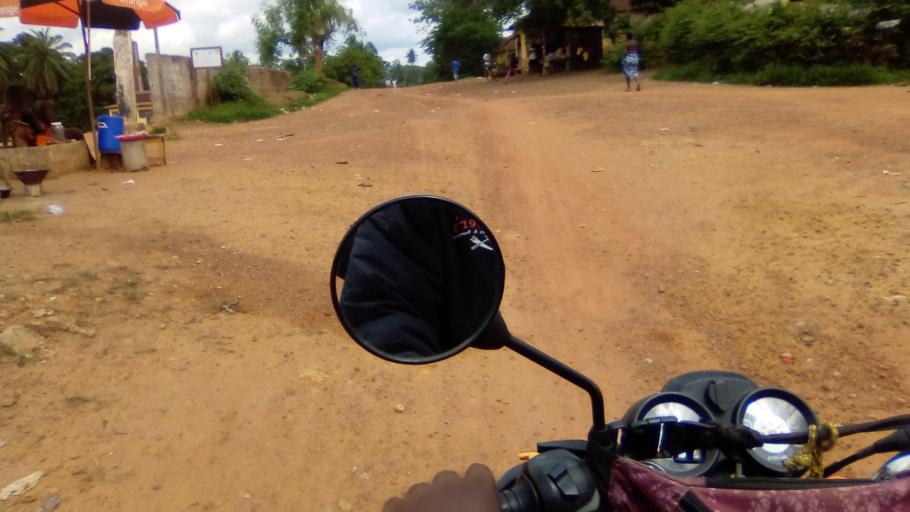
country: SL
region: Southern Province
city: Bo
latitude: 7.9630
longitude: -11.7304
